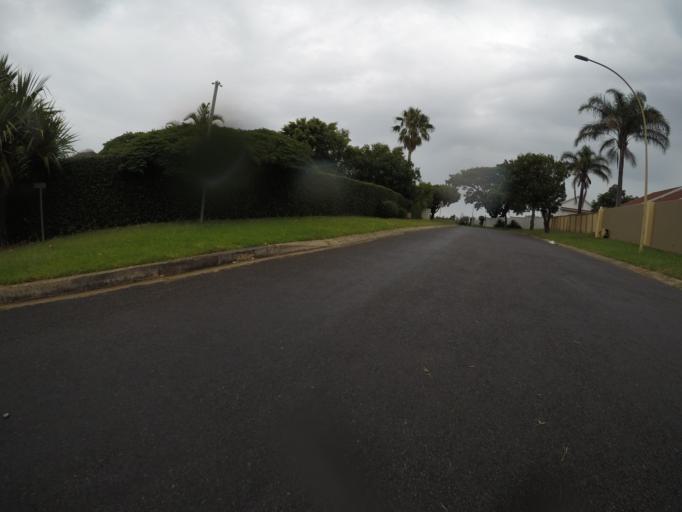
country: ZA
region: Eastern Cape
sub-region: Buffalo City Metropolitan Municipality
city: East London
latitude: -32.9897
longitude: 27.8490
